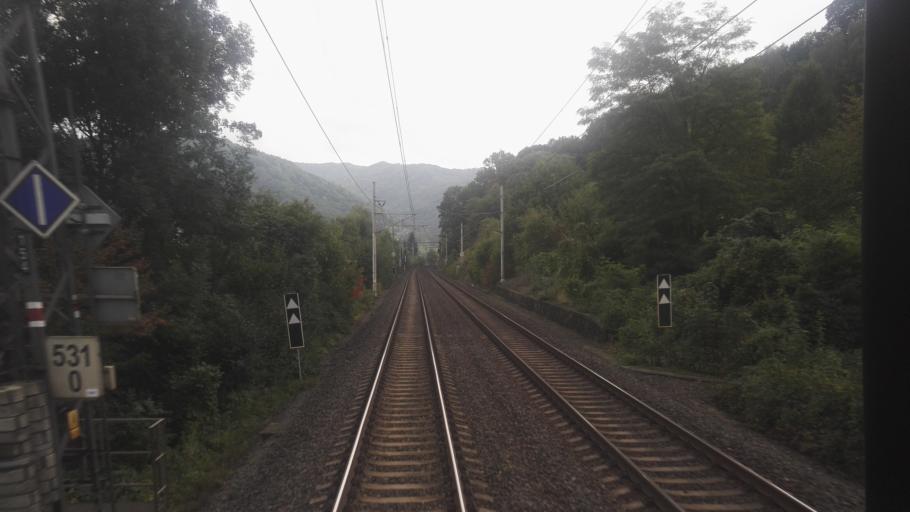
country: CZ
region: Ustecky
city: Povrly
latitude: 50.6998
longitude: 14.1974
